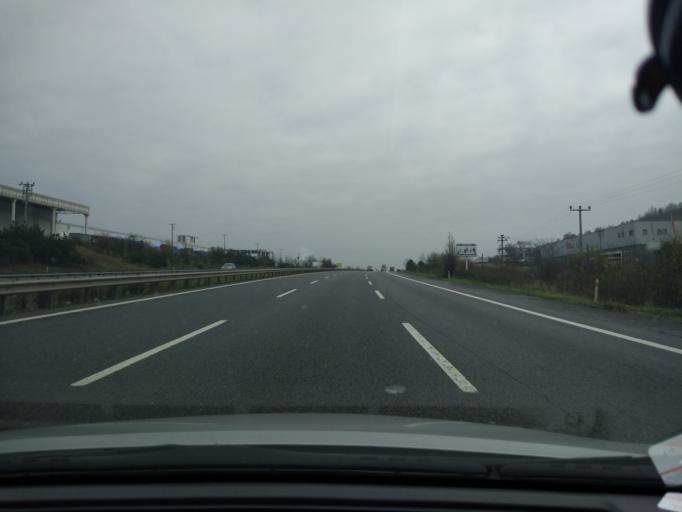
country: TR
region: Duzce
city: Gumusova
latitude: 40.8393
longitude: 30.9538
